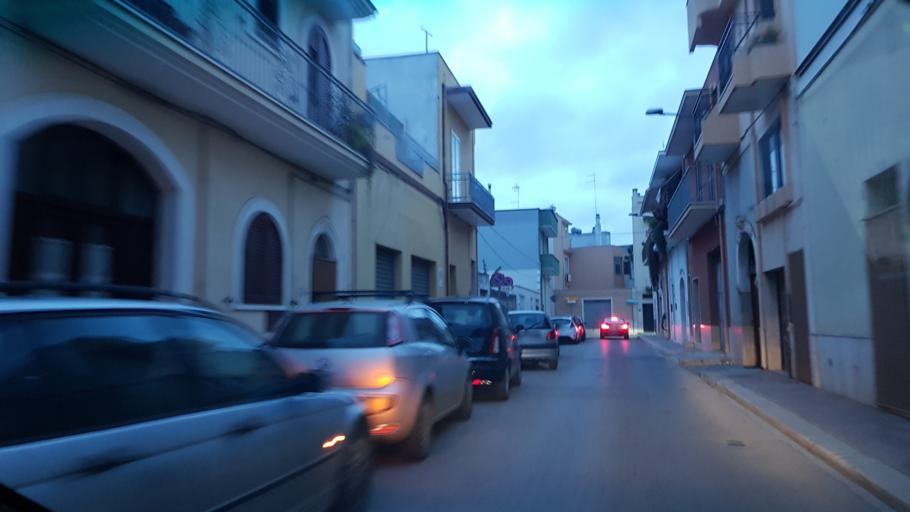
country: IT
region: Apulia
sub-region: Provincia di Brindisi
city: San Vito dei Normanni
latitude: 40.6560
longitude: 17.7087
